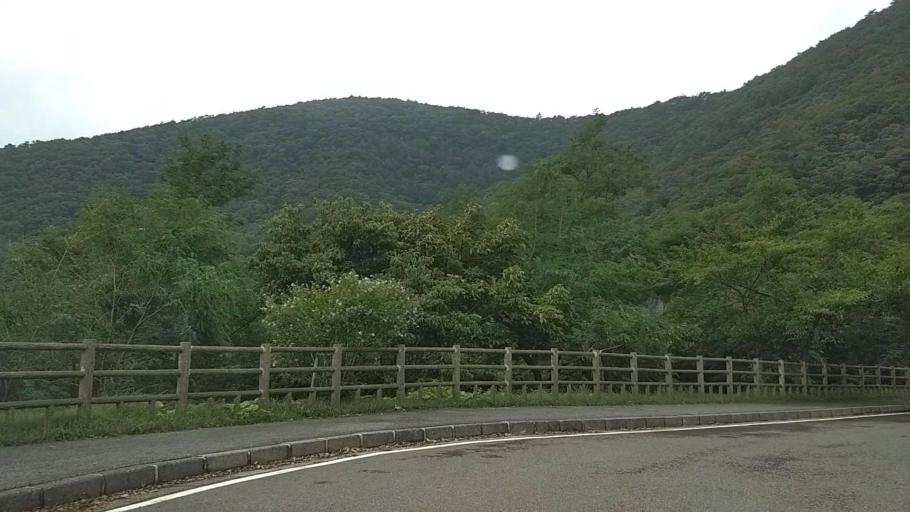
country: JP
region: Yamanashi
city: Fujikawaguchiko
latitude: 35.4740
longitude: 138.5755
